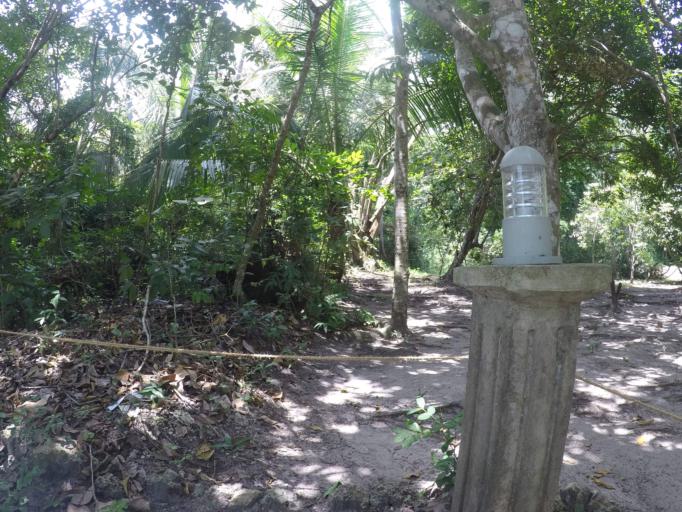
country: TZ
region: Zanzibar North
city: Mkokotoni
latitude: -5.9918
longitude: 39.1859
